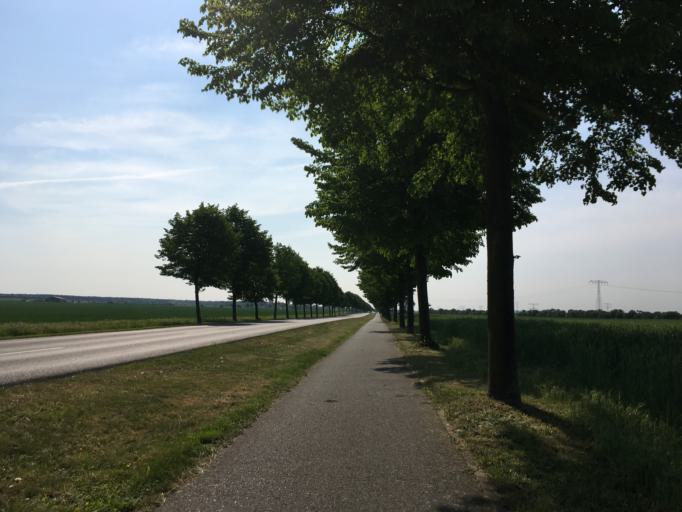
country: DE
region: Berlin
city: Falkenberg
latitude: 52.5984
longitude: 13.5376
